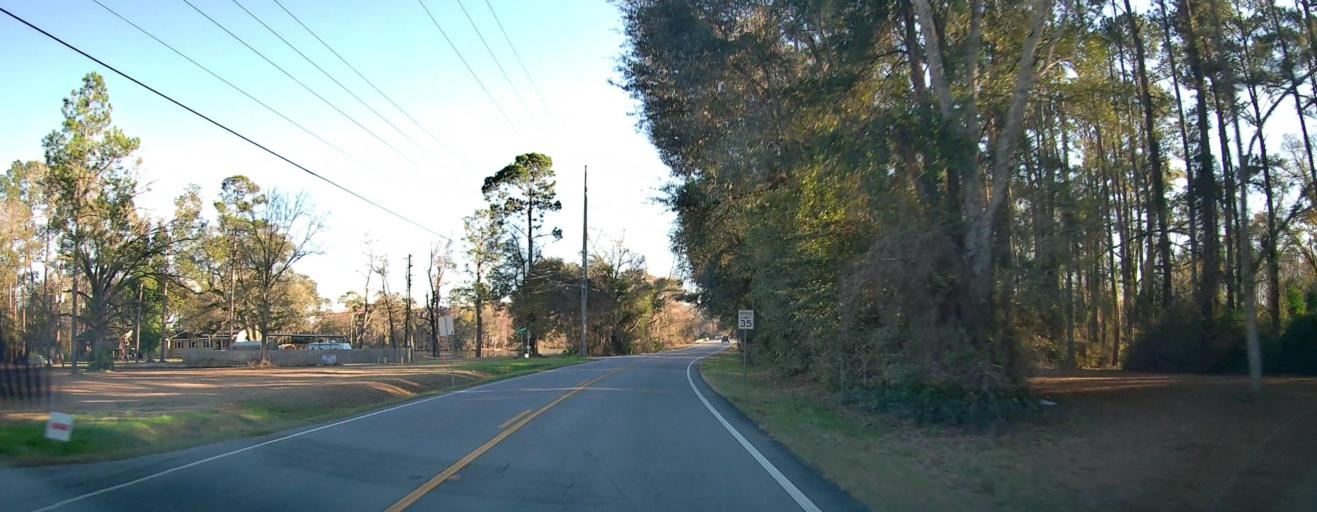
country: US
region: Georgia
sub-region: Dougherty County
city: Albany
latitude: 31.6159
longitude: -84.1595
